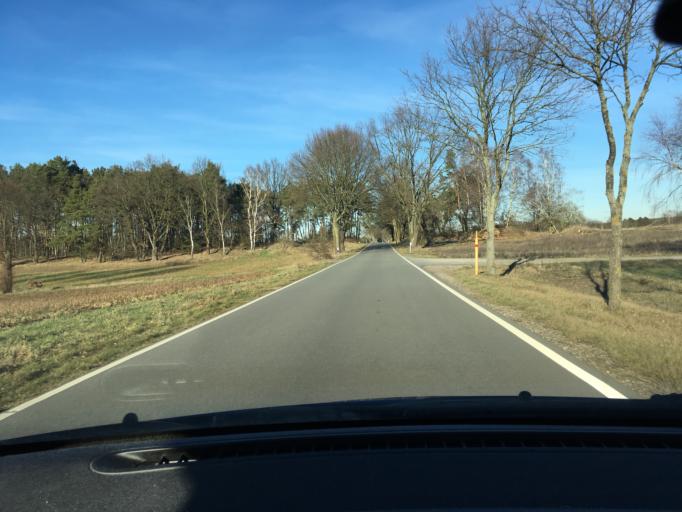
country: DE
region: Lower Saxony
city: Barnstedt
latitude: 53.1503
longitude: 10.3775
